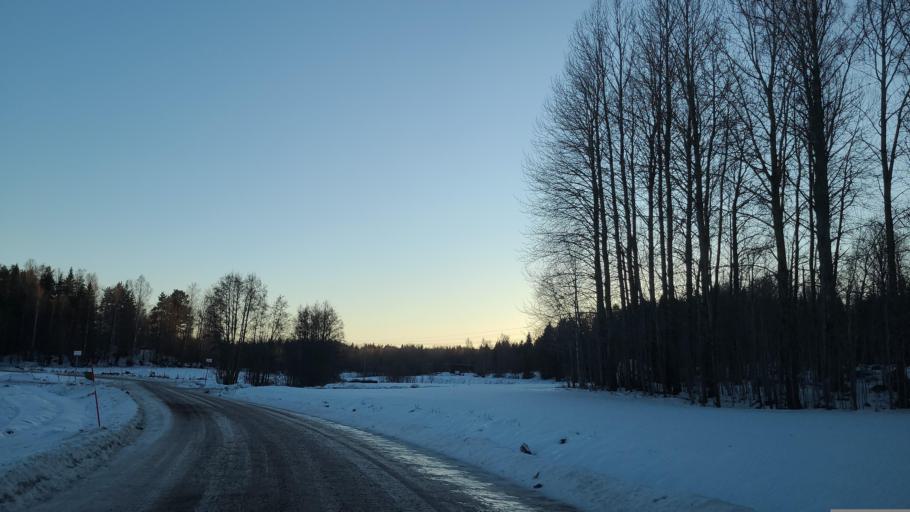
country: SE
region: Gaevleborg
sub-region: Soderhamns Kommun
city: Soderhamn
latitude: 61.2705
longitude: 16.9959
